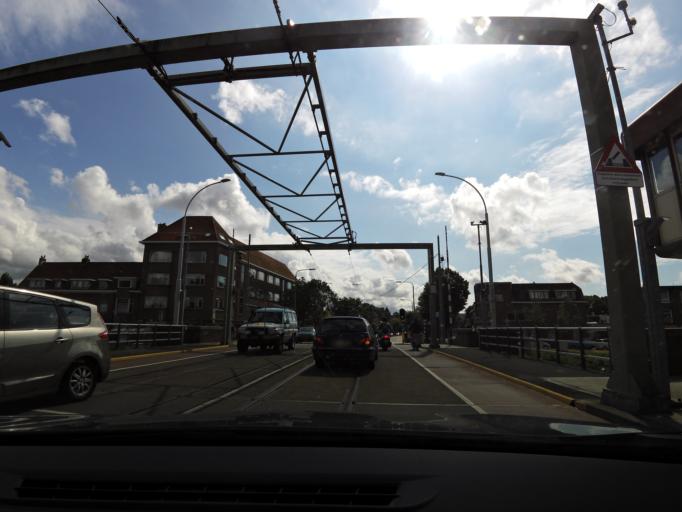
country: NL
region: South Holland
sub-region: Gemeente Leidschendam-Voorburg
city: Voorburg
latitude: 52.0596
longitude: 4.3444
